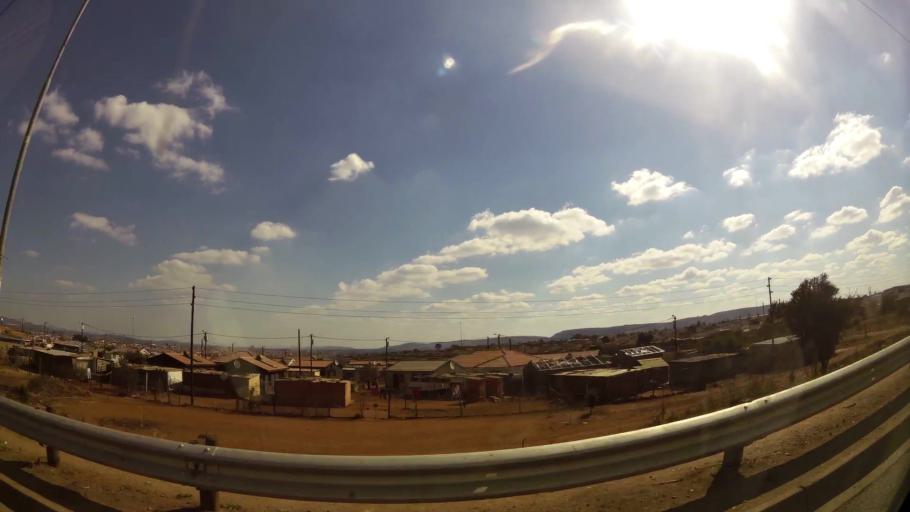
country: ZA
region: Gauteng
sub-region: City of Tshwane Metropolitan Municipality
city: Cullinan
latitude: -25.7311
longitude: 28.3993
